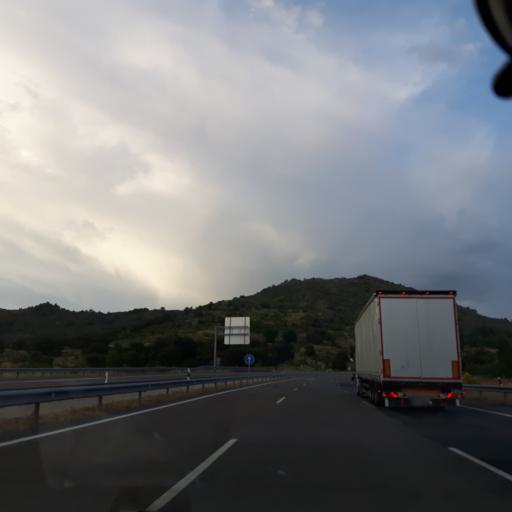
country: ES
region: Castille and Leon
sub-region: Provincia de Salamanca
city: Fresnedoso
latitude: 40.4341
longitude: -5.6946
